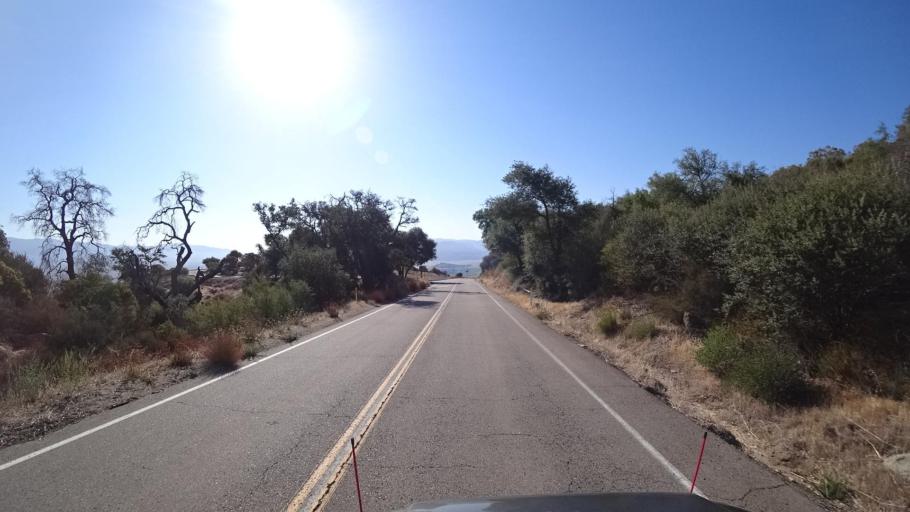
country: US
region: California
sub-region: Riverside County
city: Aguanga
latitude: 33.2560
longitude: -116.7609
